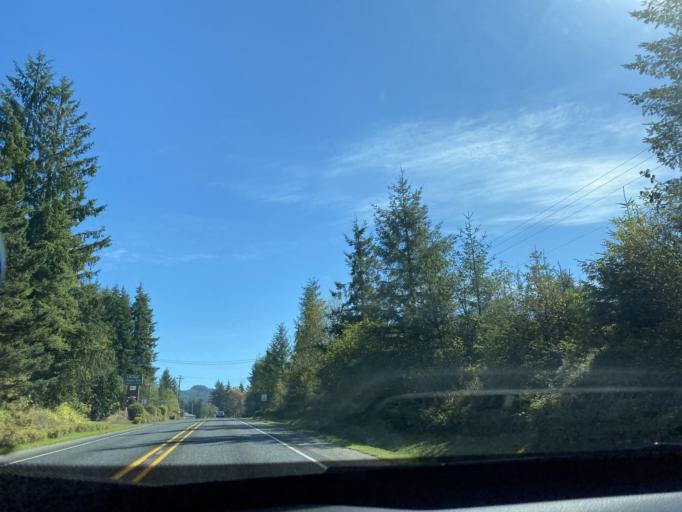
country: US
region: Washington
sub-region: Clallam County
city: Forks
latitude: 47.9586
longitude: -124.3908
